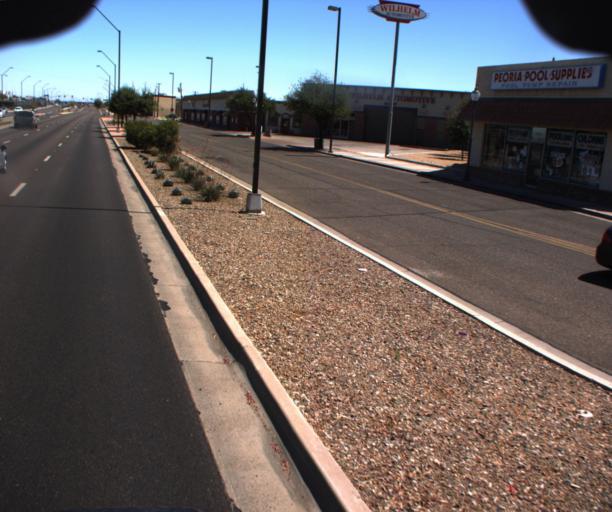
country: US
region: Arizona
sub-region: Maricopa County
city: Peoria
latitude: 33.5806
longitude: -112.2368
